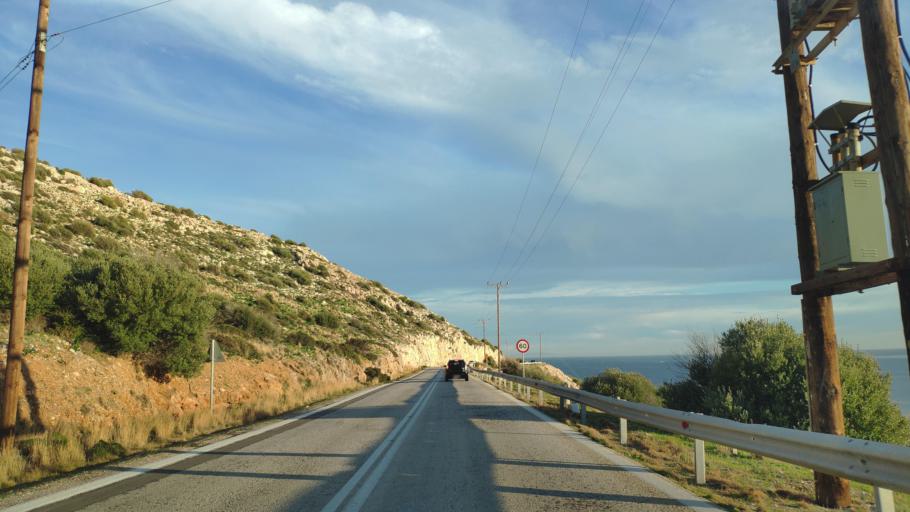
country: GR
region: Attica
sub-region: Nomarchia Anatolikis Attikis
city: Palaia Fokaia
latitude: 37.6709
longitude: 23.9485
